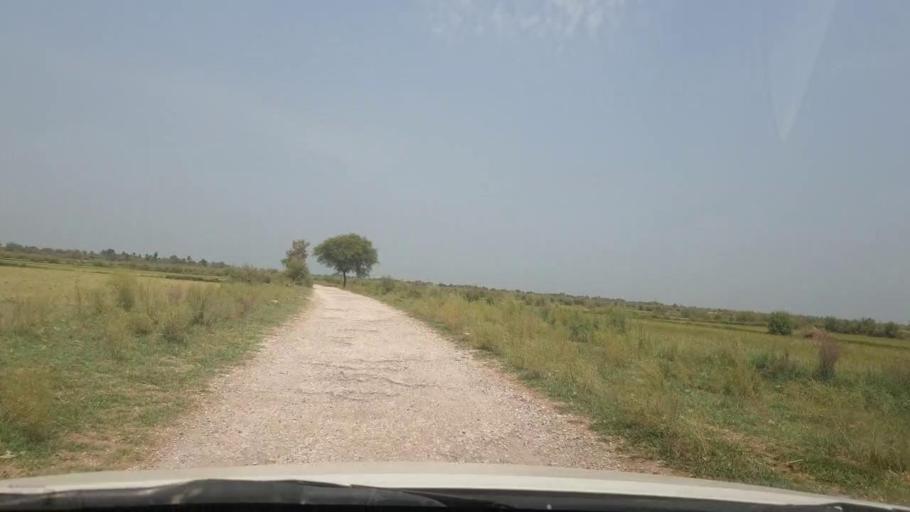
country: PK
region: Sindh
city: Rustam jo Goth
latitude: 28.0522
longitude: 68.7515
